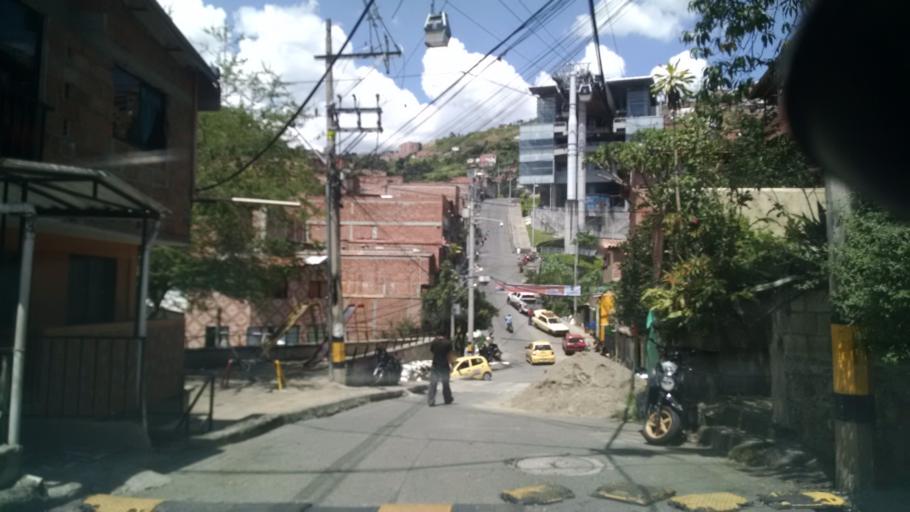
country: CO
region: Antioquia
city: Medellin
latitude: 6.2643
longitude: -75.6135
